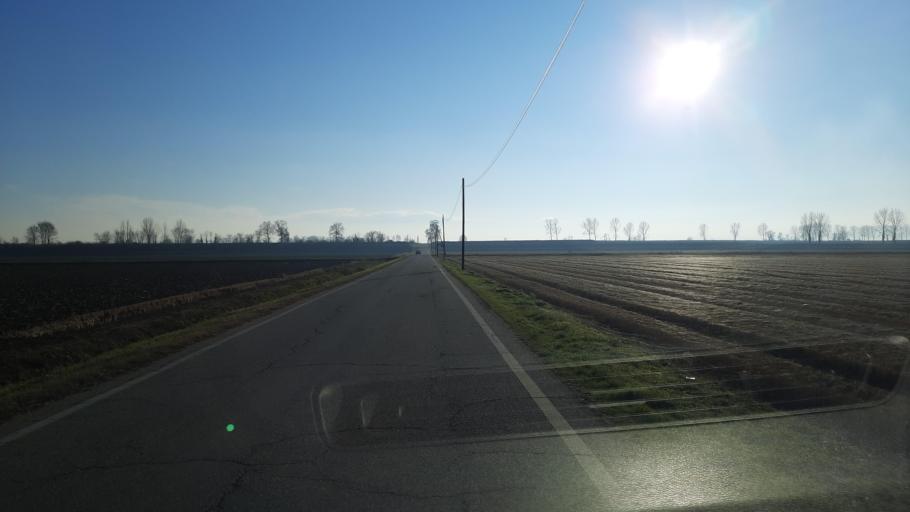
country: IT
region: Piedmont
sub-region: Provincia di Vercelli
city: Costanzana
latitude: 45.2153
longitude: 8.3634
